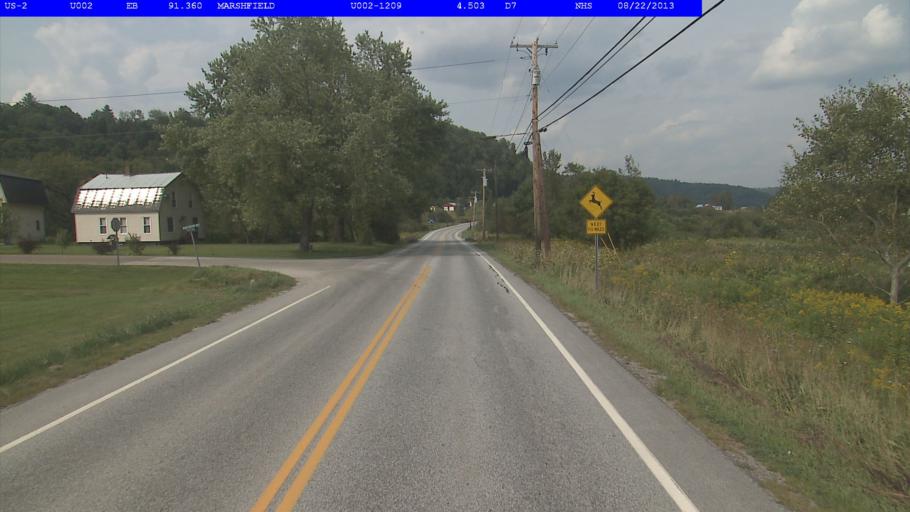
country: US
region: Vermont
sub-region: Caledonia County
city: Hardwick
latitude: 44.3295
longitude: -72.3764
